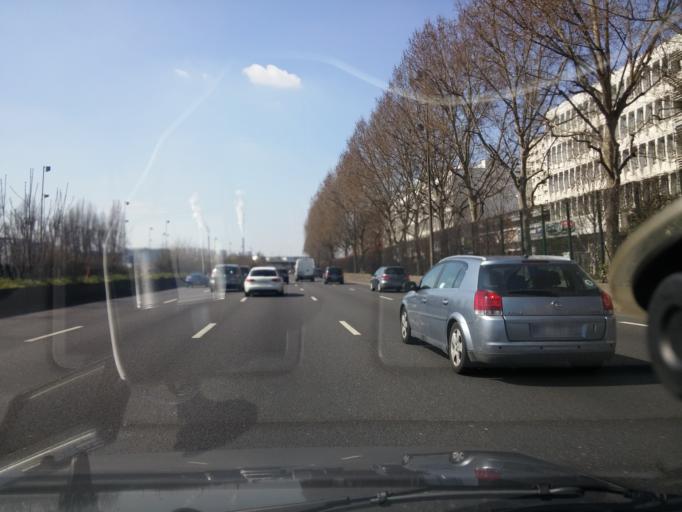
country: FR
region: Ile-de-France
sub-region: Departement du Val-de-Marne
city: Charenton-le-Pont
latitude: 48.8192
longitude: 2.4070
